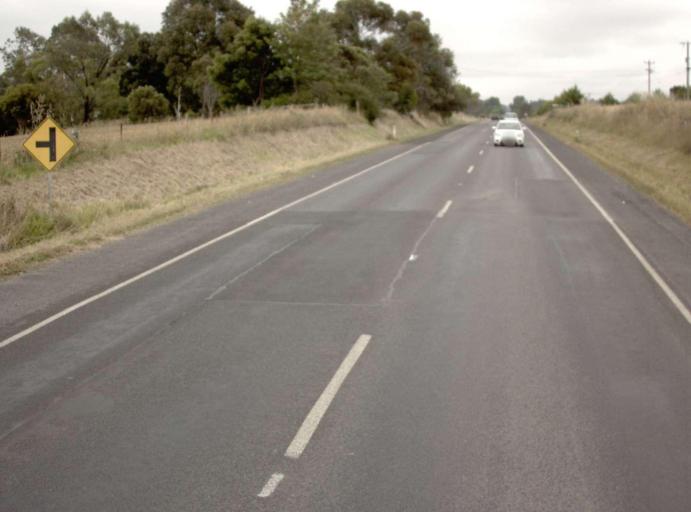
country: AU
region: Victoria
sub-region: Latrobe
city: Morwell
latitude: -38.2990
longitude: 146.4181
